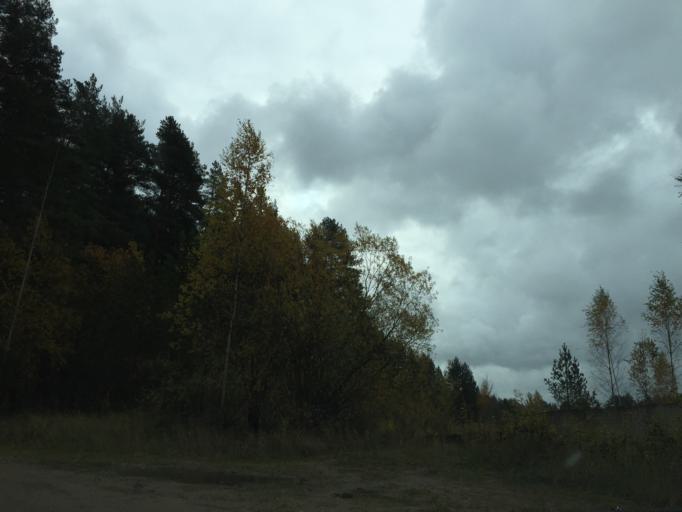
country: LV
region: Ogre
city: Ogre
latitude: 56.8003
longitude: 24.6454
